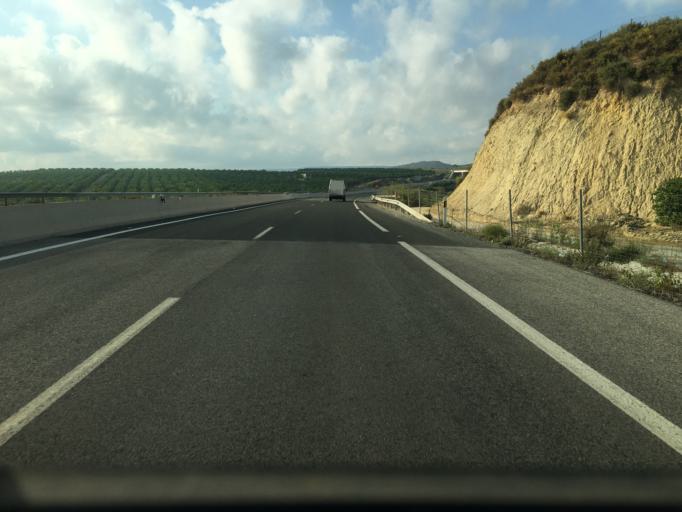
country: ES
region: Murcia
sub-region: Murcia
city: Beniel
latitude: 37.9927
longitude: -0.9762
